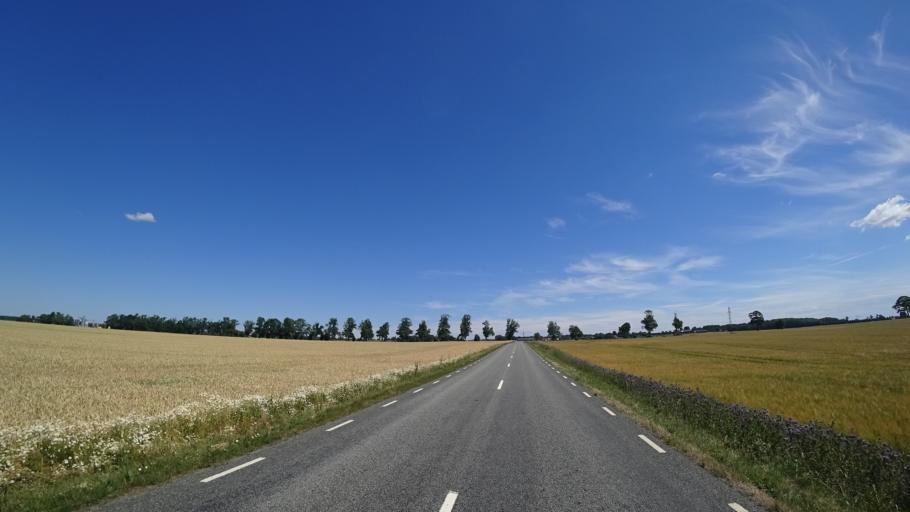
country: SE
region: Skane
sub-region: Kristianstads Kommun
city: Onnestad
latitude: 56.0673
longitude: 14.0599
